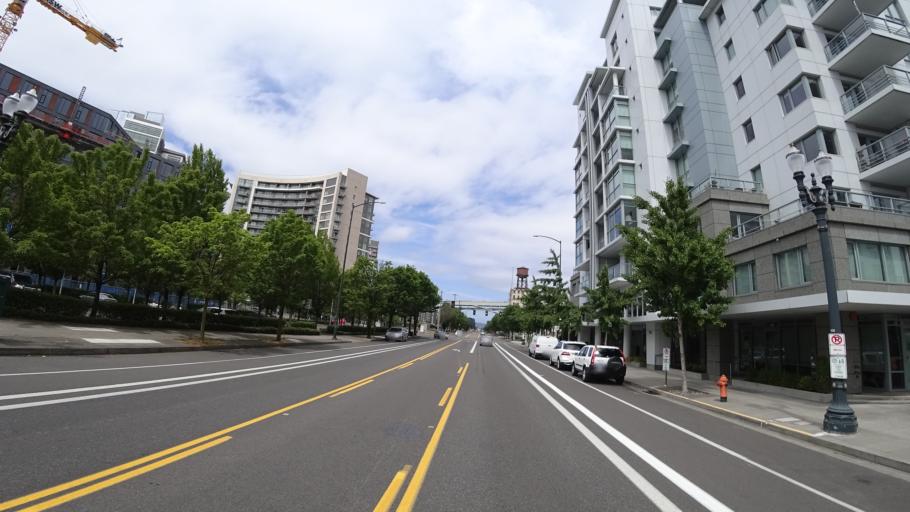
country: US
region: Oregon
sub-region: Multnomah County
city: Portland
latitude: 45.5324
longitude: -122.6789
